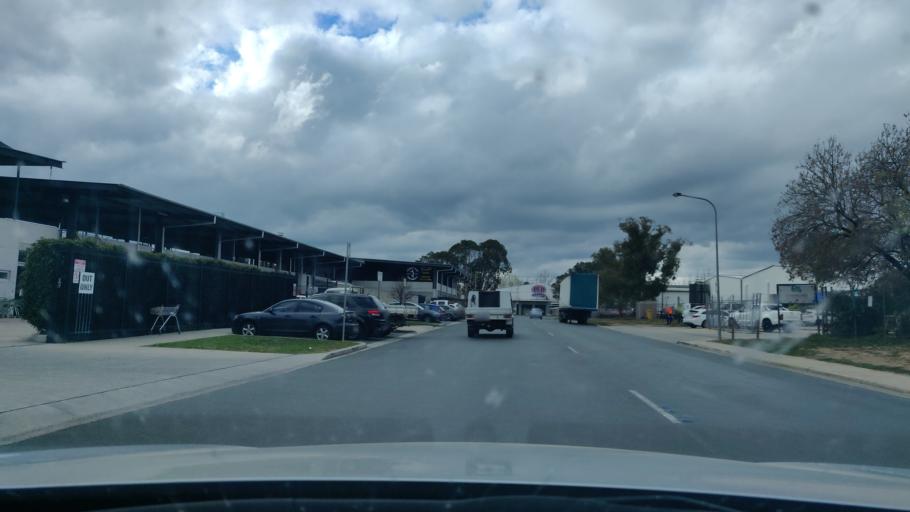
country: AU
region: Australian Capital Territory
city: Forrest
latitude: -35.3249
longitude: 149.1555
